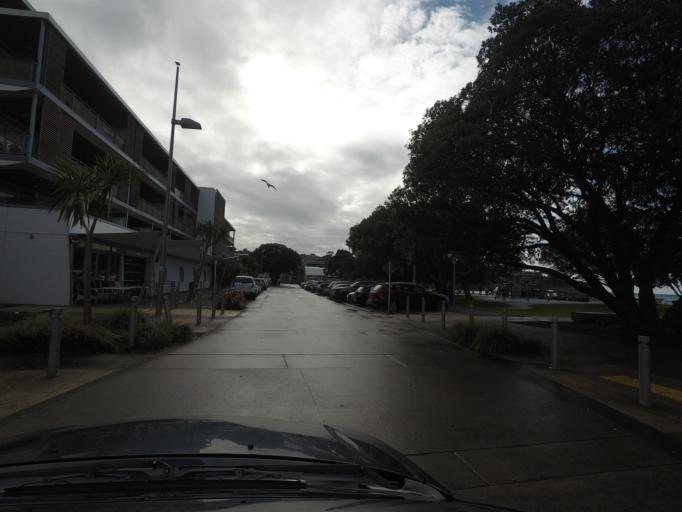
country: NZ
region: Auckland
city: Murrays Bay
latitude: -36.7143
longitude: 174.7489
